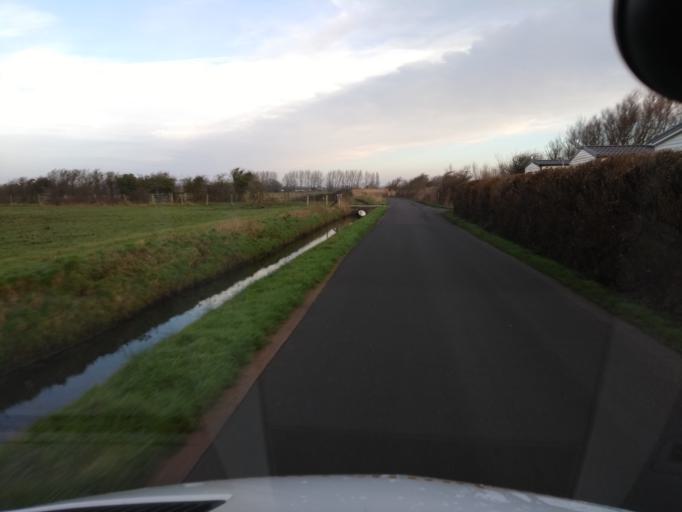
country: GB
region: England
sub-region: Somerset
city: Burnham-on-Sea
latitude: 51.2722
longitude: -3.0041
